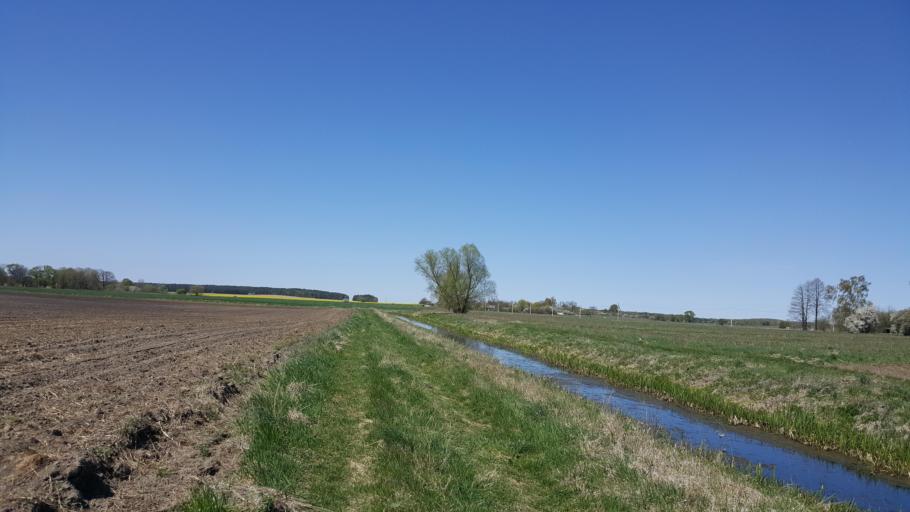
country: BY
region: Brest
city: Charnawchytsy
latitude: 52.3166
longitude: 23.7154
